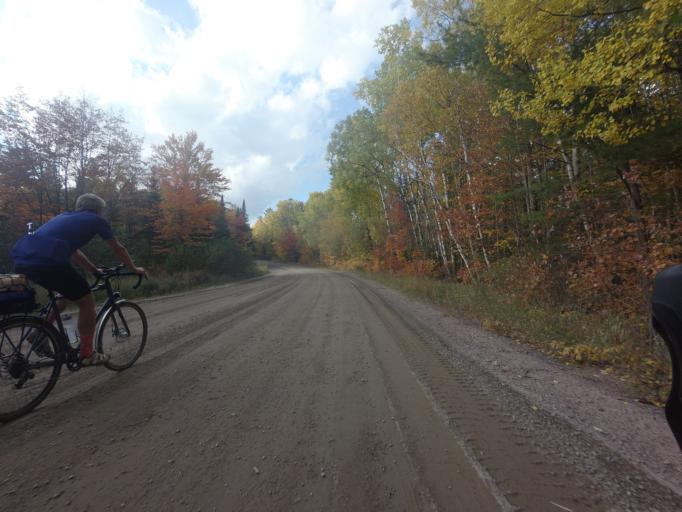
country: CA
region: Ontario
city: Petawawa
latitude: 45.8376
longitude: -77.5010
